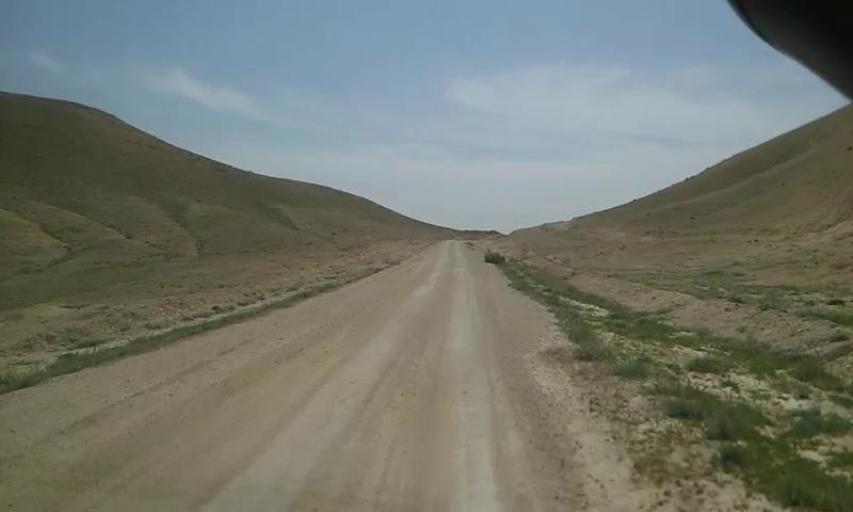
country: PS
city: `Arab ar Rashaydah
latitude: 31.4970
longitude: 35.2938
